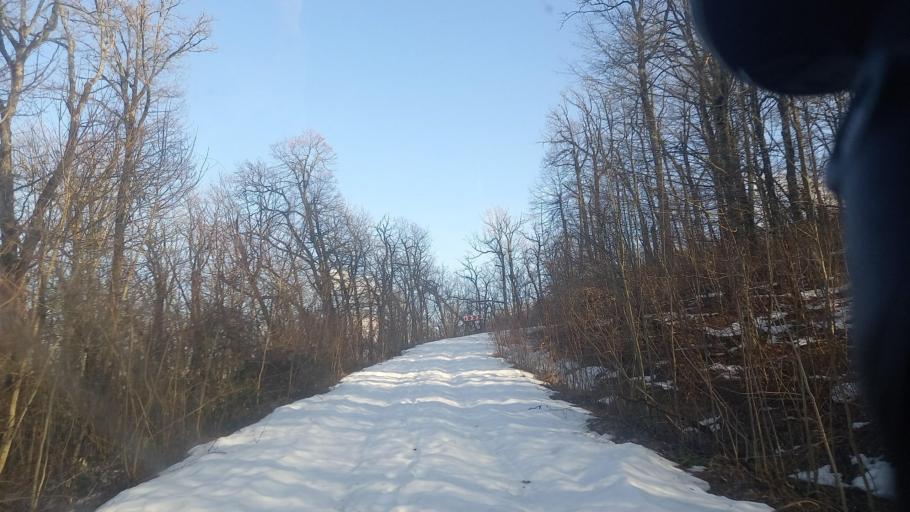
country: RU
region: Krasnodarskiy
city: Smolenskaya
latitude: 44.6687
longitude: 38.7968
